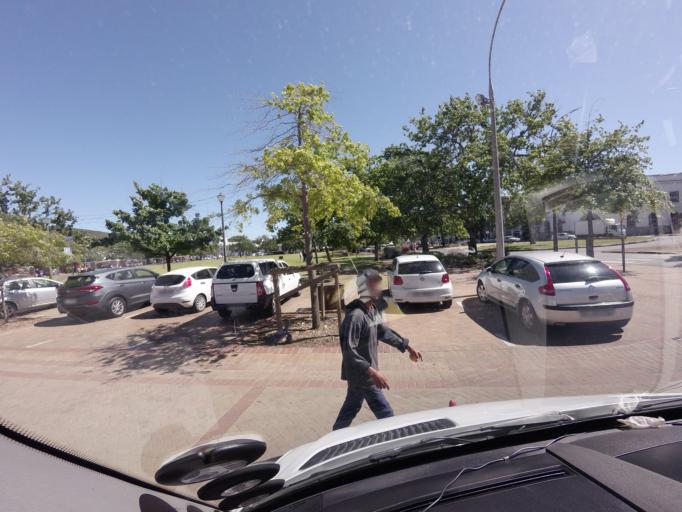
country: ZA
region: Western Cape
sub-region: Cape Winelands District Municipality
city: Stellenbosch
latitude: -33.9376
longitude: 18.8593
